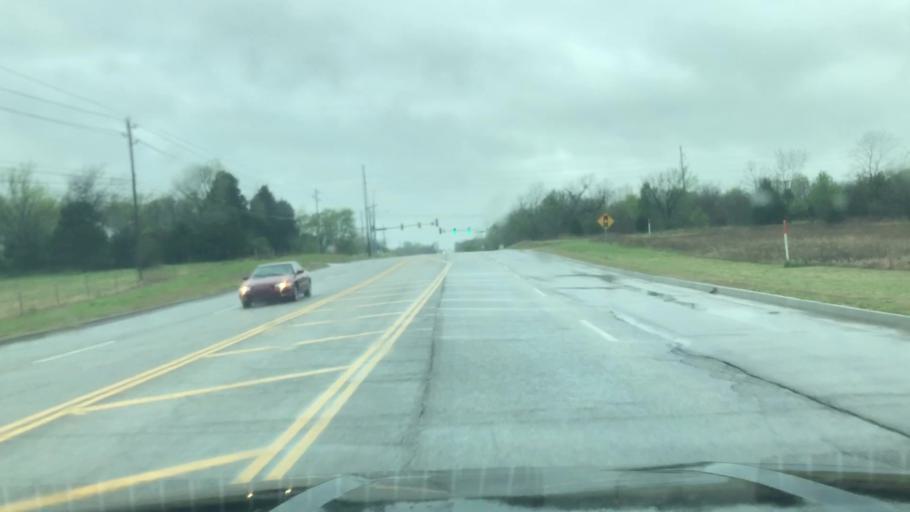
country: US
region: Oklahoma
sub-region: Tulsa County
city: Owasso
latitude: 36.2641
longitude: -95.8999
